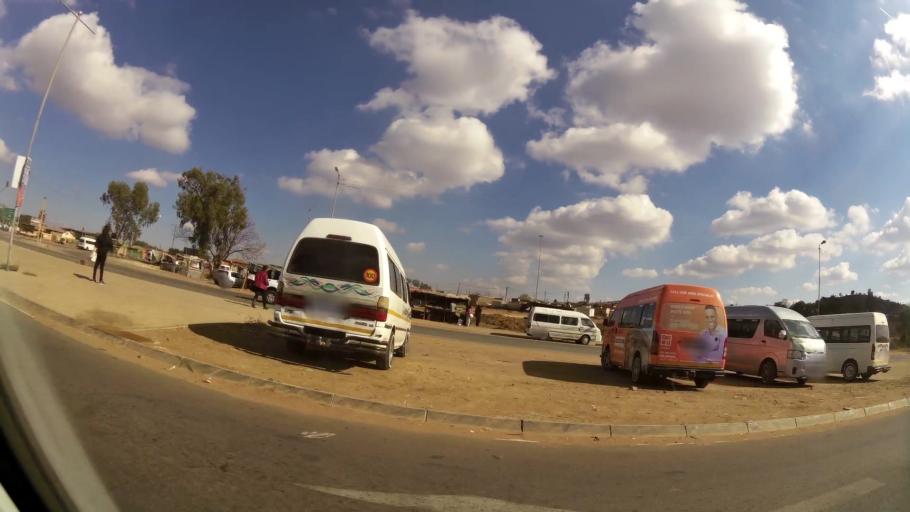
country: ZA
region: Gauteng
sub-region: City of Tshwane Metropolitan Municipality
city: Cullinan
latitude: -25.6978
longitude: 28.4199
